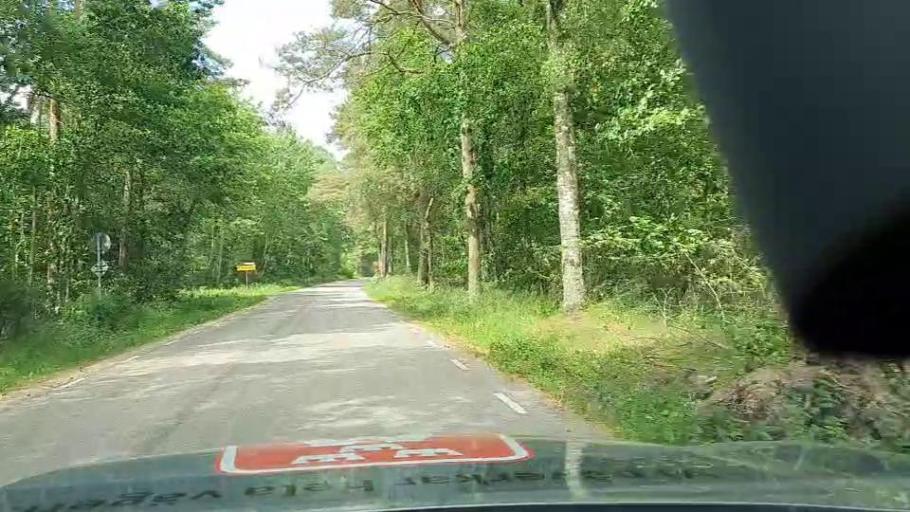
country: SE
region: Blekinge
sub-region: Karlshamns Kommun
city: Morrum
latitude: 56.1012
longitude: 14.6862
